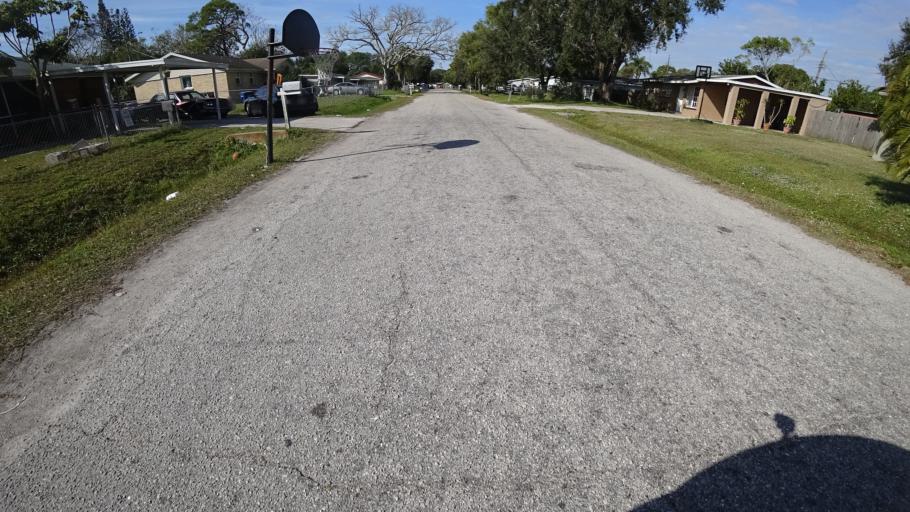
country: US
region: Florida
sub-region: Manatee County
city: Whitfield
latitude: 27.4356
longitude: -82.5656
